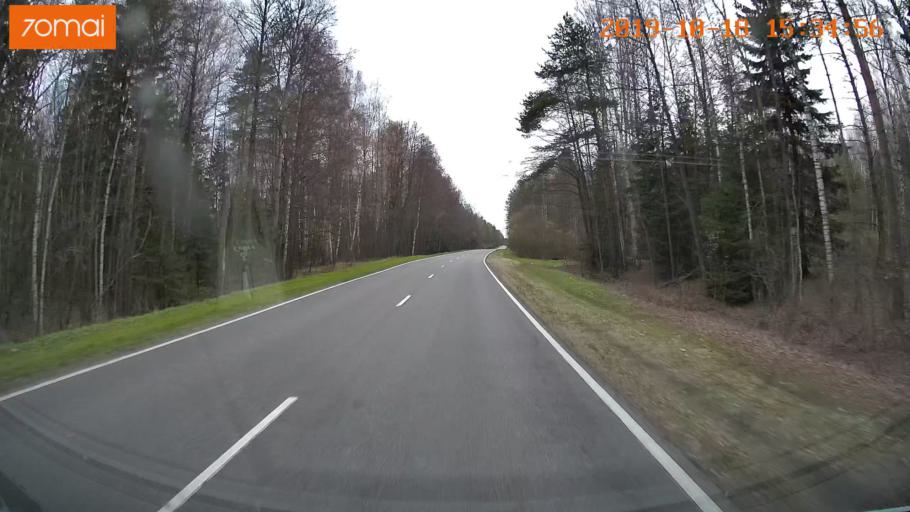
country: RU
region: Vladimir
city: Anopino
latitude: 55.8610
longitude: 40.6365
